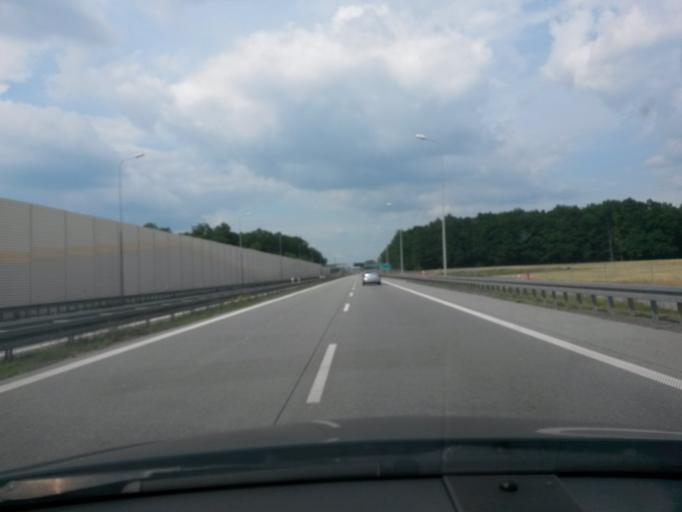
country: PL
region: Lodz Voivodeship
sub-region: Powiat rawski
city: Rawa Mazowiecka
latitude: 51.8060
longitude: 20.3033
